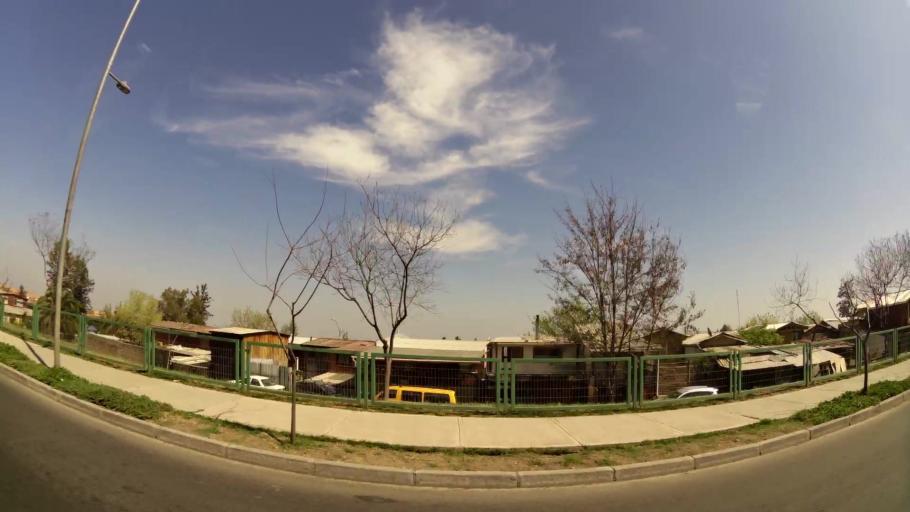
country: CL
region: Santiago Metropolitan
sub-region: Provincia de Santiago
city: Villa Presidente Frei, Nunoa, Santiago, Chile
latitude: -33.4573
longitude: -70.5295
